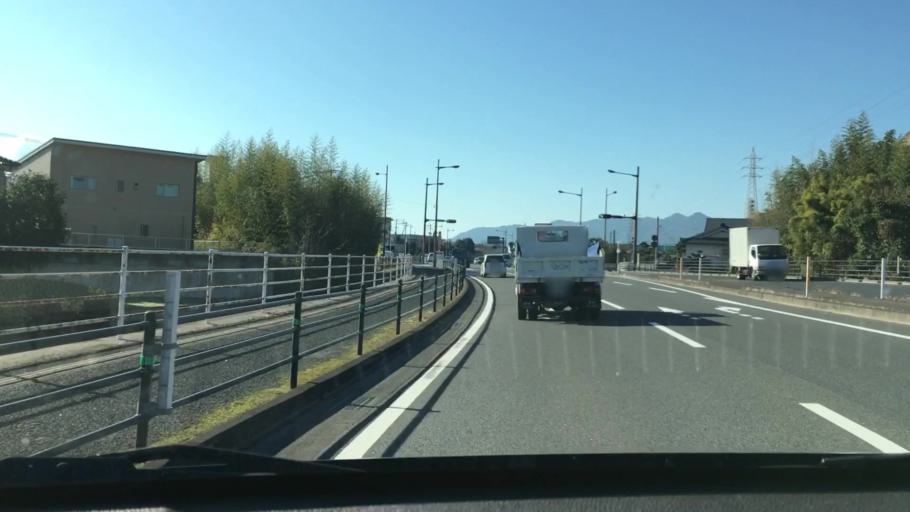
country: JP
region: Kagoshima
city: Kajiki
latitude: 31.7413
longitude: 130.6525
